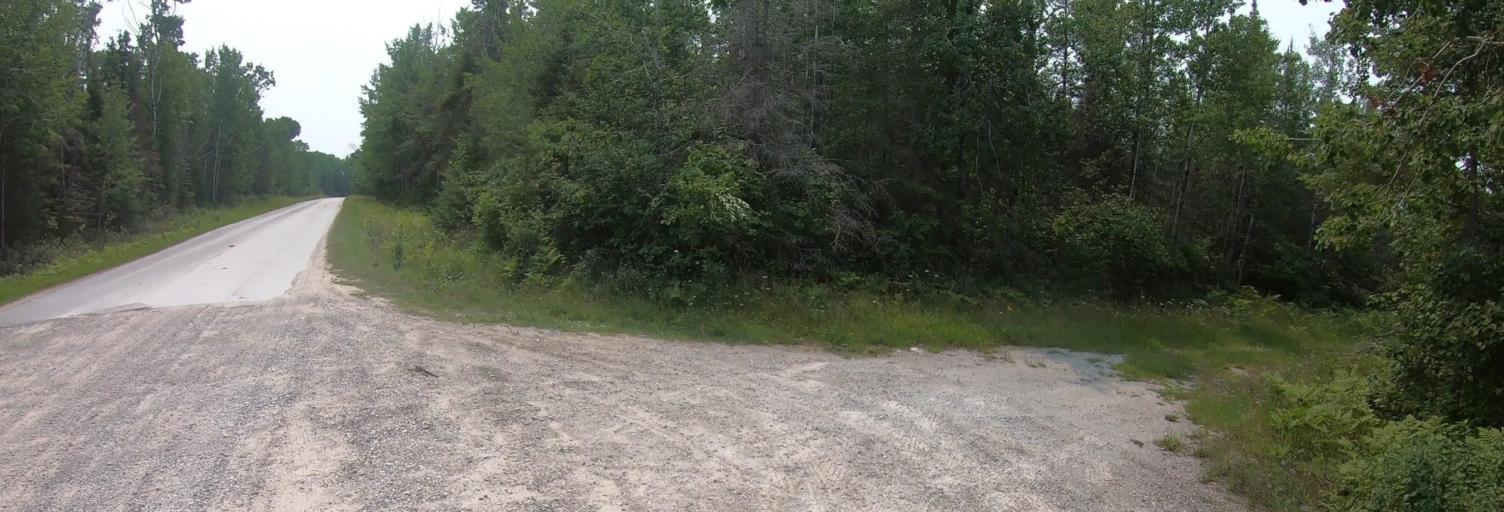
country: CA
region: Ontario
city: Thessalon
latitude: 46.0675
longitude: -83.6648
